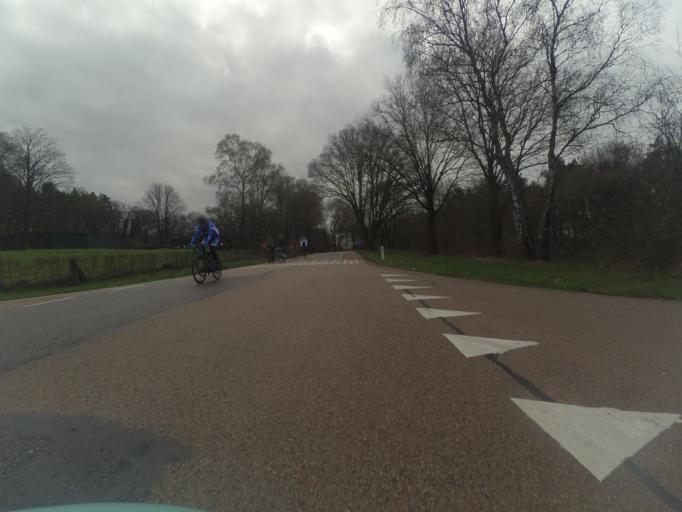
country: NL
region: Gelderland
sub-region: Gemeente Arnhem
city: Hoogkamp
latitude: 52.0628
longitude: 5.8960
